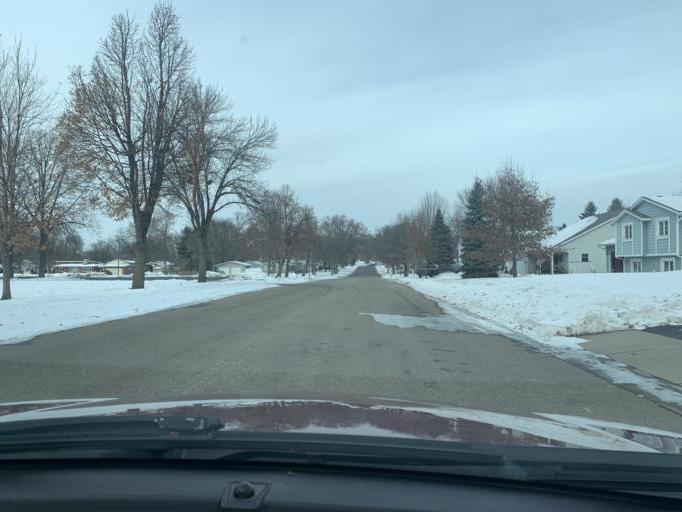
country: US
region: Minnesota
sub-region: Washington County
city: Saint Paul Park
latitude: 44.8410
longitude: -92.9856
